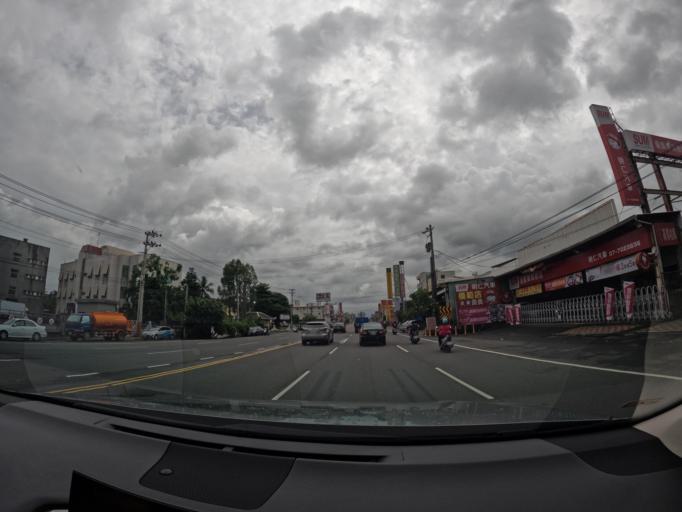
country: TW
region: Taiwan
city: Fengshan
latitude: 22.6299
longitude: 120.3833
